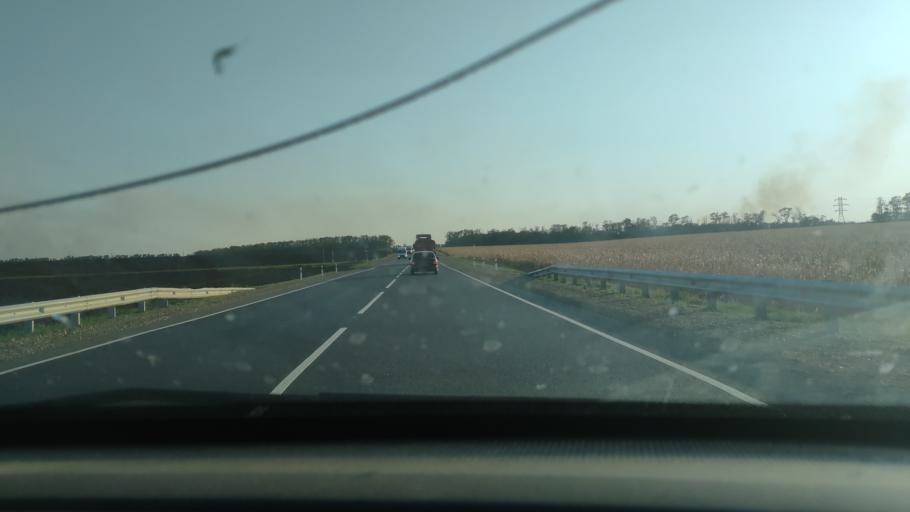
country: RU
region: Krasnodarskiy
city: Kanevskaya
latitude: 46.0443
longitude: 38.9887
